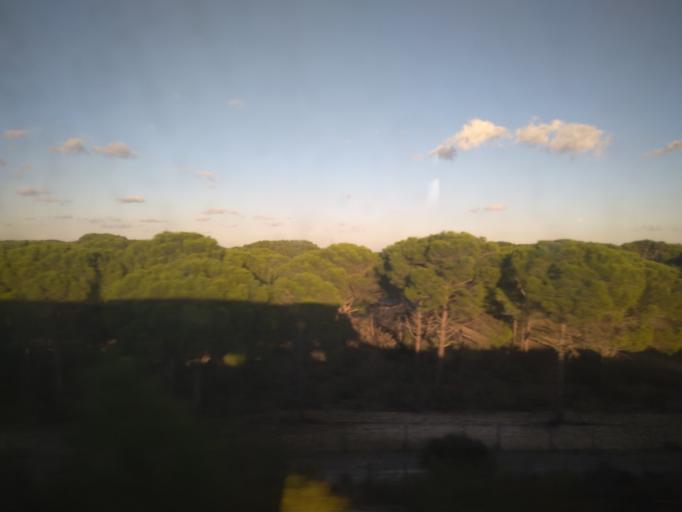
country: PT
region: Setubal
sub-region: Grandola
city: Grandola
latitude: 38.2691
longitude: -8.5434
